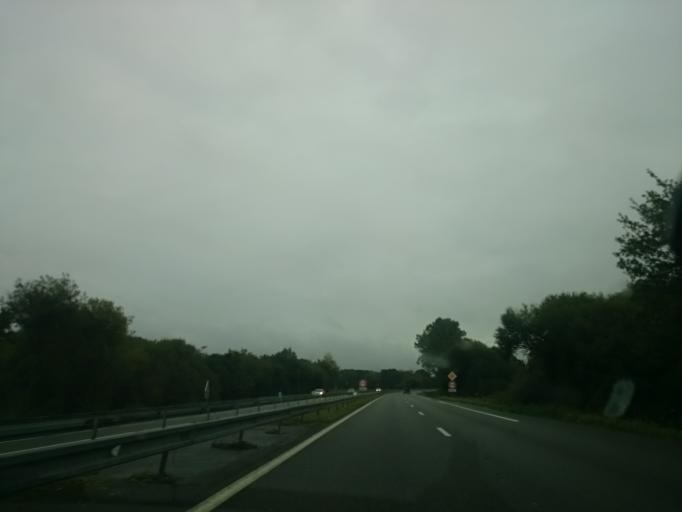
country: FR
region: Brittany
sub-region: Departement du Morbihan
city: Theix
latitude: 47.6311
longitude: -2.6439
